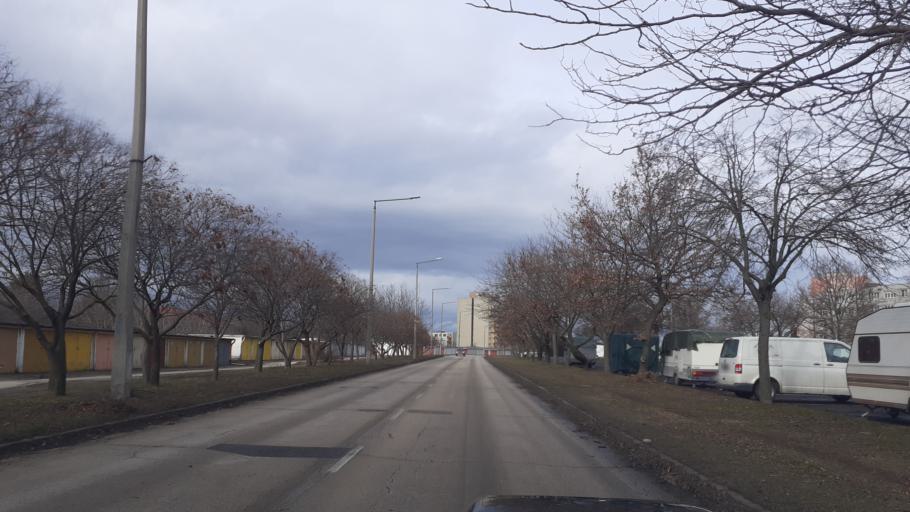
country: HU
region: Fejer
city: dunaujvaros
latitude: 46.9632
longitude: 18.9164
